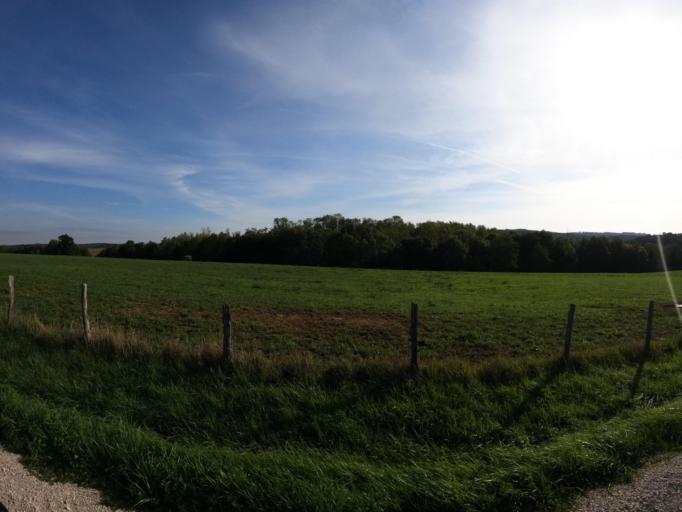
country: FR
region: Franche-Comte
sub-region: Departement du Jura
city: Bletterans
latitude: 46.7317
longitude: 5.5043
